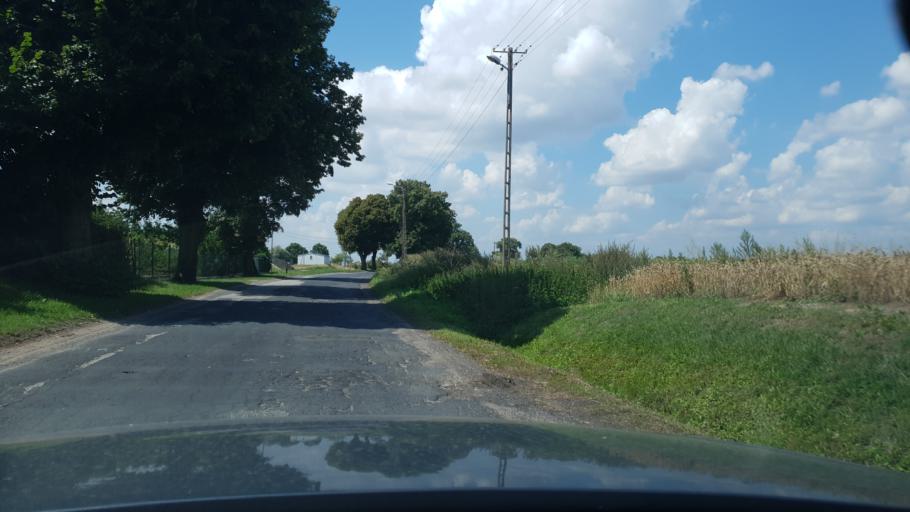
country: PL
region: Kujawsko-Pomorskie
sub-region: Powiat wabrzeski
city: Pluznica
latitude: 53.3219
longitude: 18.8345
